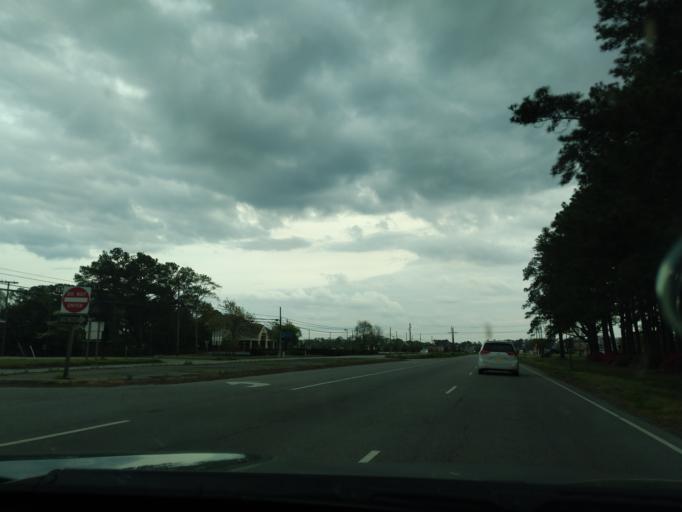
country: US
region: North Carolina
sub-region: Martin County
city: Williamston
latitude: 35.8401
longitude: -77.0643
